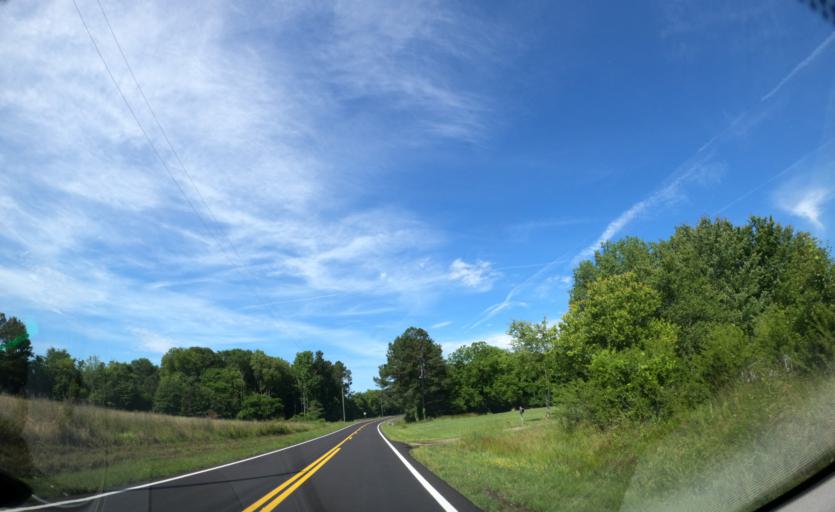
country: US
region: Georgia
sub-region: Elbert County
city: Elberton
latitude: 34.1115
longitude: -82.7483
